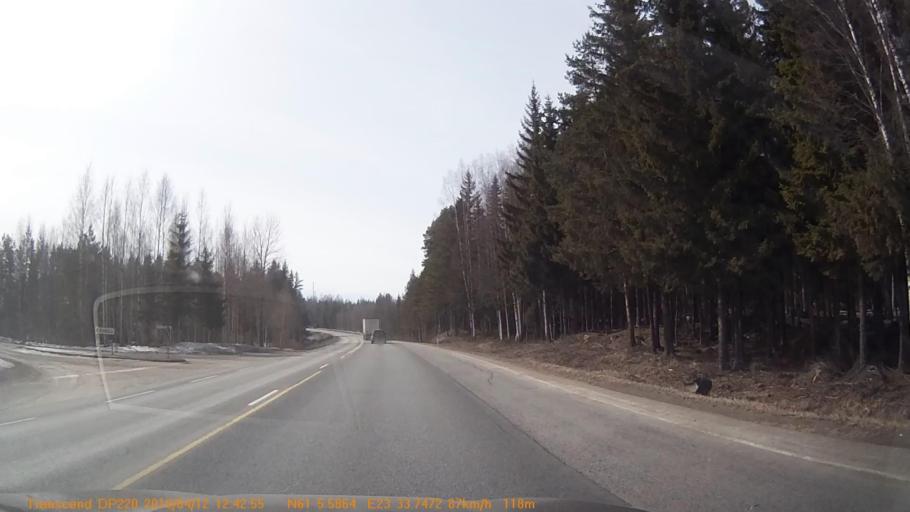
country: FI
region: Pirkanmaa
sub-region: Etelae-Pirkanmaa
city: Urjala
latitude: 61.0930
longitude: 23.5620
